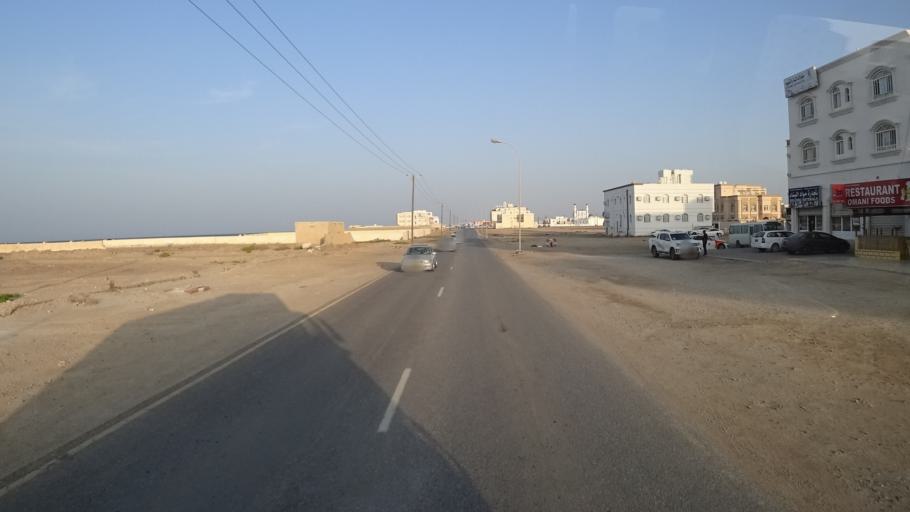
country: OM
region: Ash Sharqiyah
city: Sur
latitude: 22.6077
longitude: 59.4738
